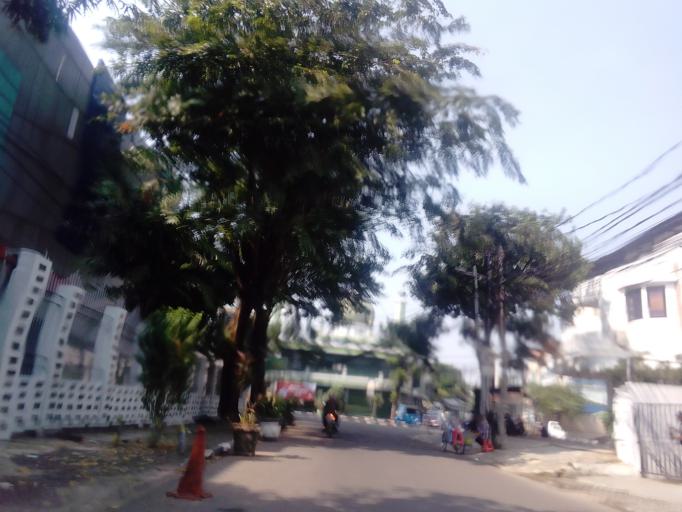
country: ID
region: Jakarta Raya
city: Jakarta
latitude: -6.2525
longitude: 106.7981
